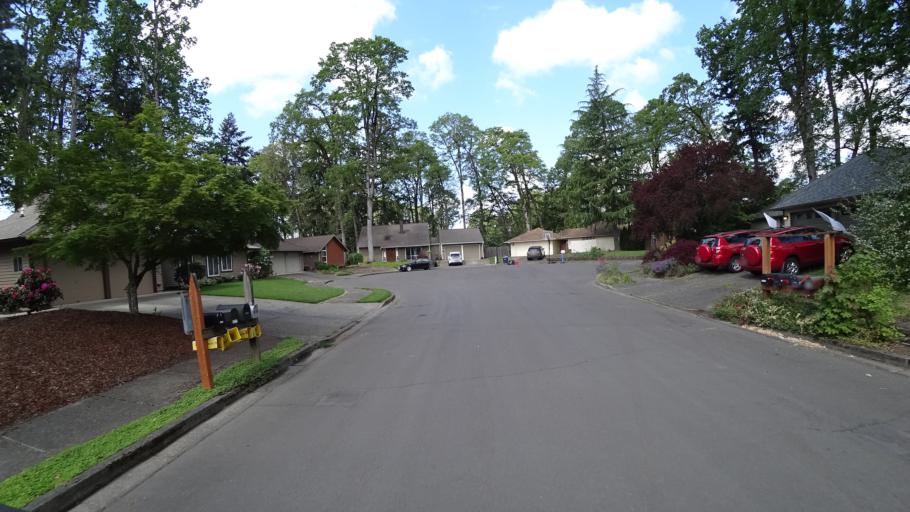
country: US
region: Oregon
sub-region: Washington County
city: Aloha
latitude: 45.5072
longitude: -122.8848
